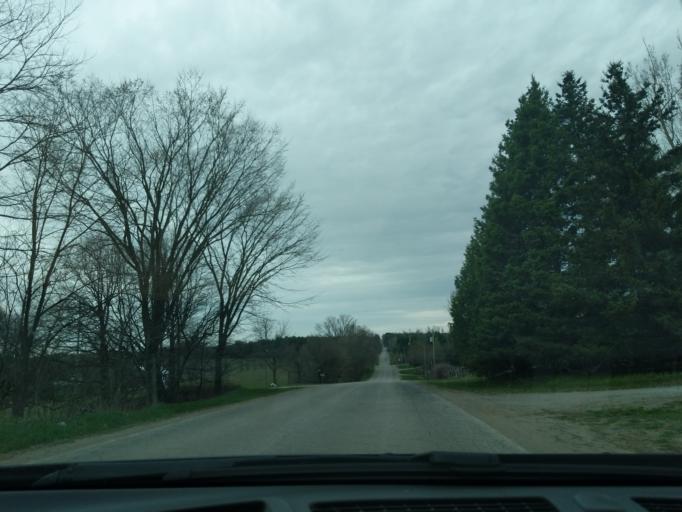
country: CA
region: Ontario
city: Orangeville
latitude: 44.0113
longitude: -79.9665
